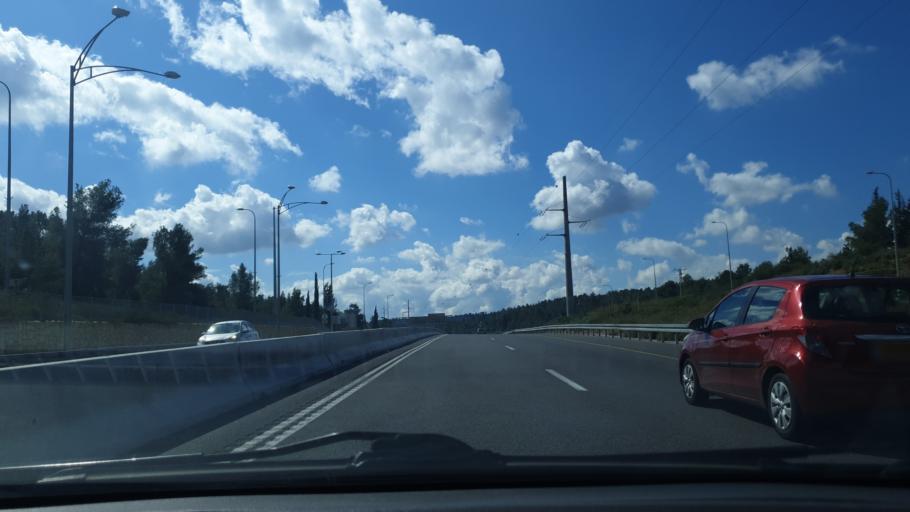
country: IL
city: Mevo horon
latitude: 31.8131
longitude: 35.0215
